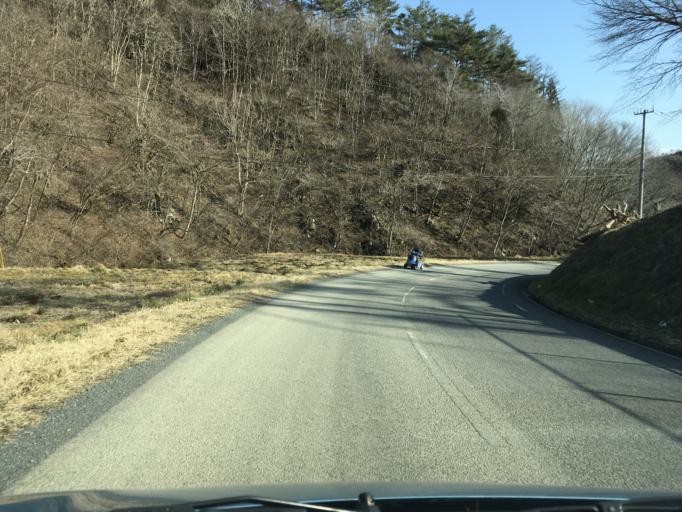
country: JP
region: Iwate
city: Ichinoseki
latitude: 38.7912
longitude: 141.4507
